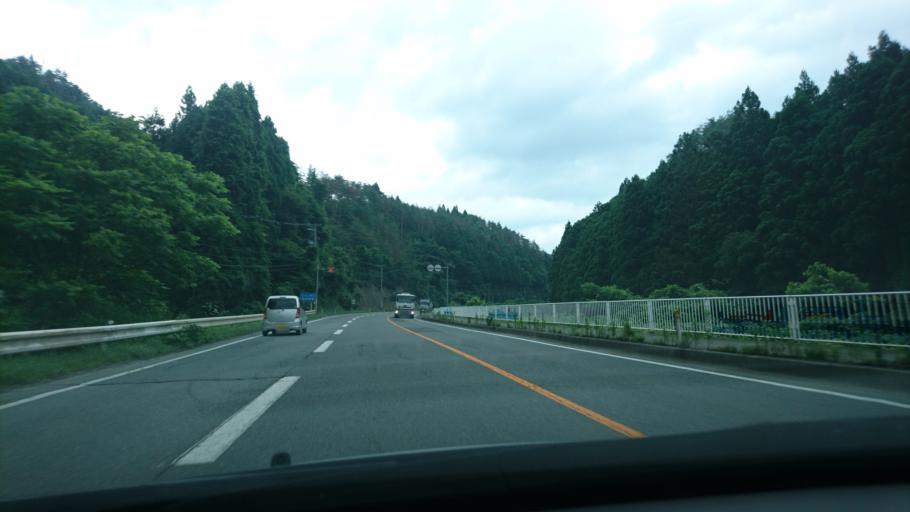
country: JP
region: Iwate
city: Ofunato
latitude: 38.9236
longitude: 141.5931
